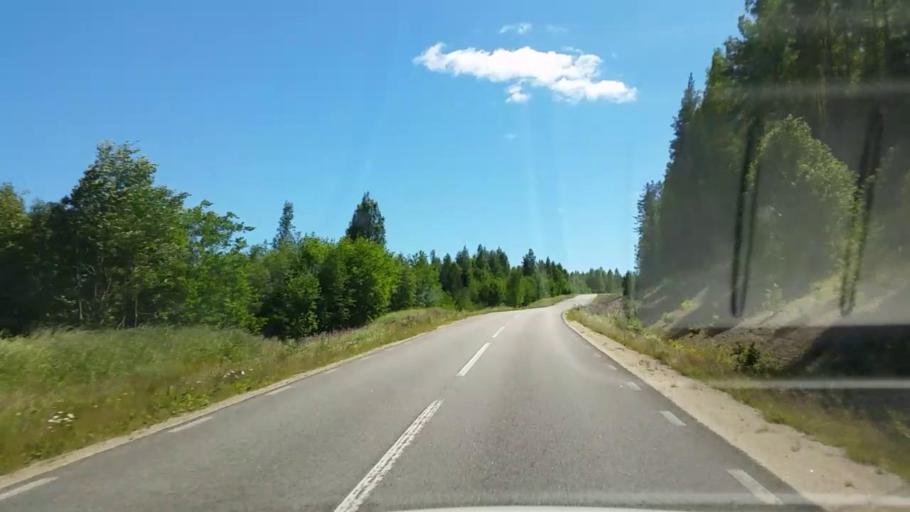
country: SE
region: Gaevleborg
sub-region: Ljusdals Kommun
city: Farila
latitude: 61.6940
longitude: 15.6488
